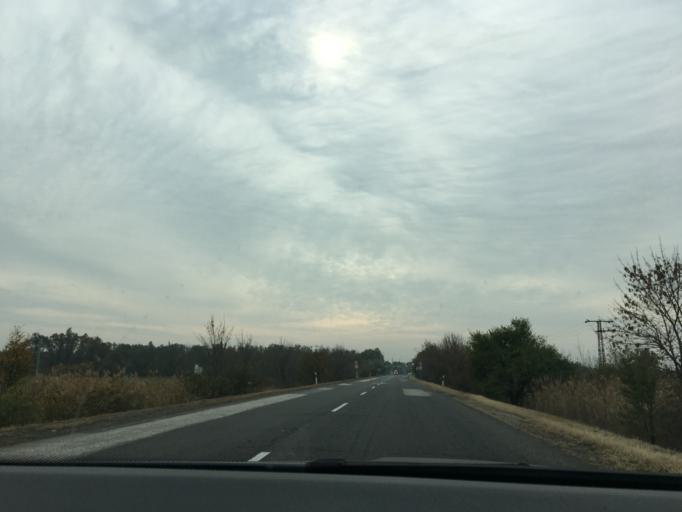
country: HU
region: Jasz-Nagykun-Szolnok
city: Karcag
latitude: 47.3003
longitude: 20.9332
